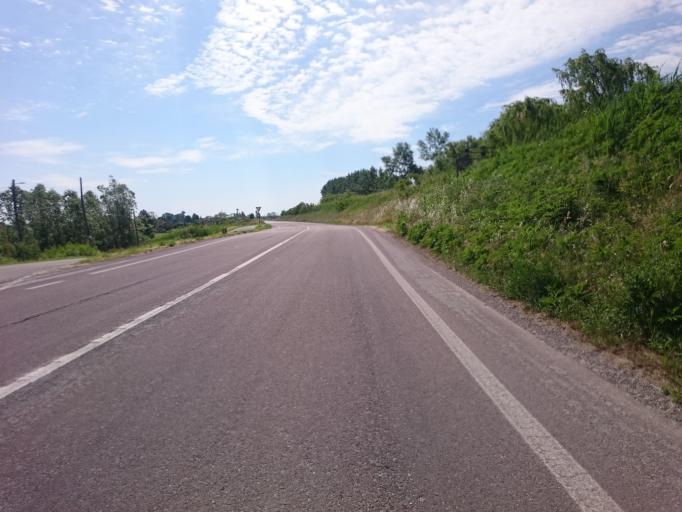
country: IT
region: Veneto
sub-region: Provincia di Rovigo
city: Ariano
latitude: 44.9592
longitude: 12.1158
